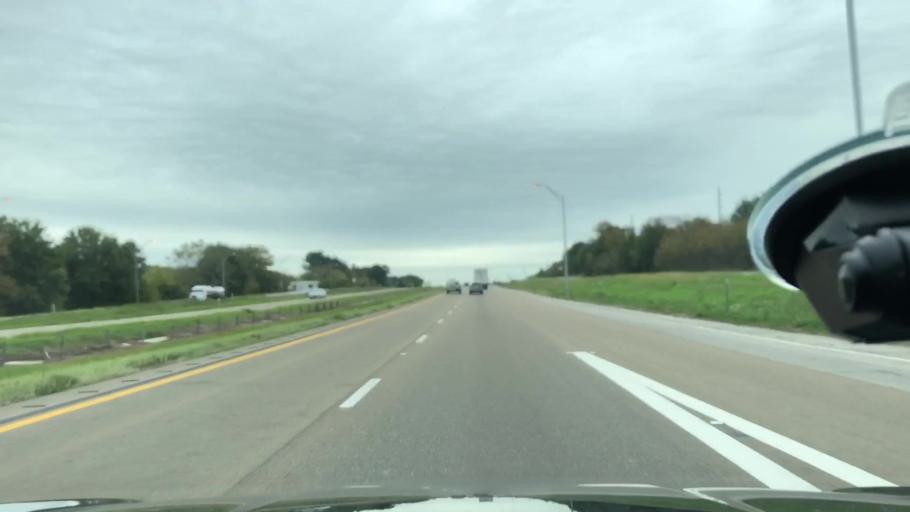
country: US
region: Texas
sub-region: Titus County
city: Mount Pleasant
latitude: 33.1585
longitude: -95.0468
